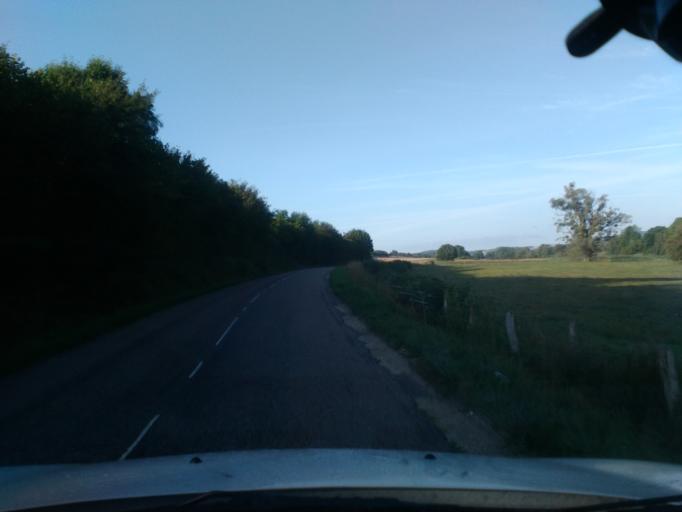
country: FR
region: Lorraine
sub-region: Departement des Vosges
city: Mirecourt
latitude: 48.3035
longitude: 6.0873
